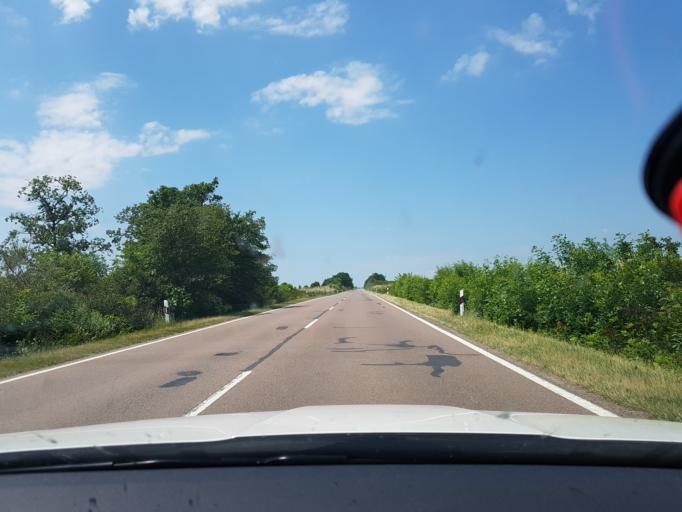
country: HU
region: Hajdu-Bihar
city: Hortobagy
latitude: 47.5874
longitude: 21.1031
